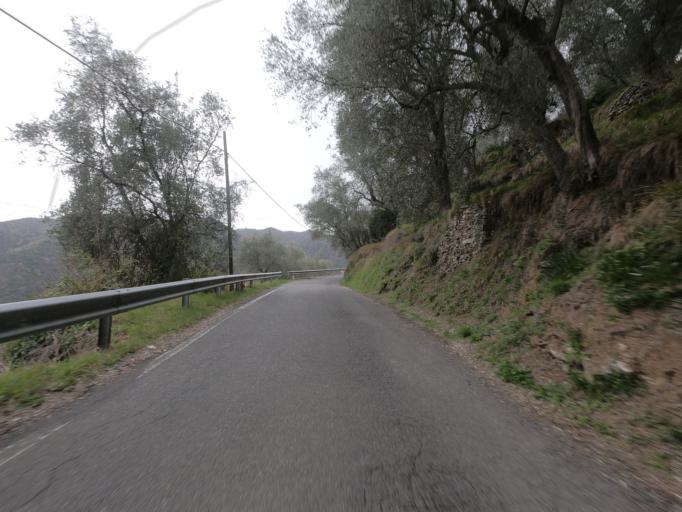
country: IT
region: Liguria
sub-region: Provincia di Savona
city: Casanova Lerrone
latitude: 44.0341
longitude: 8.0270
